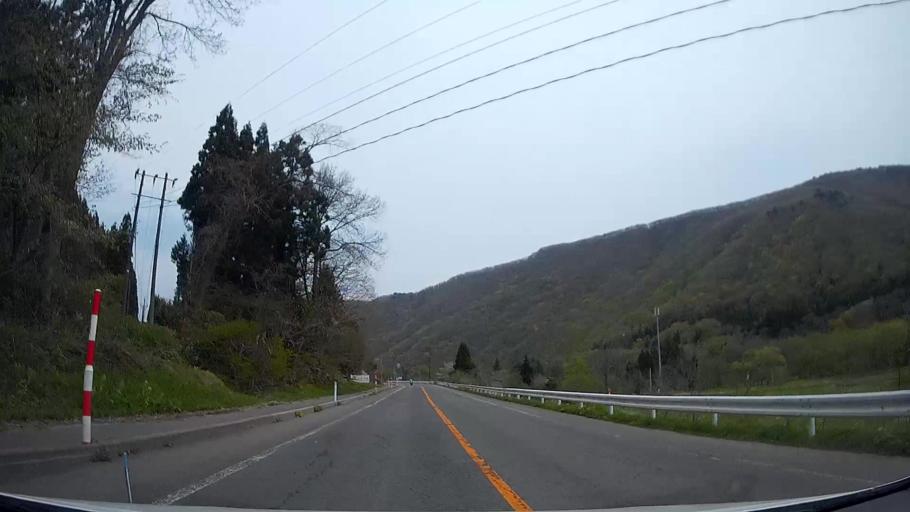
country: JP
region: Akita
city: Hanawa
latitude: 40.3461
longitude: 140.8377
